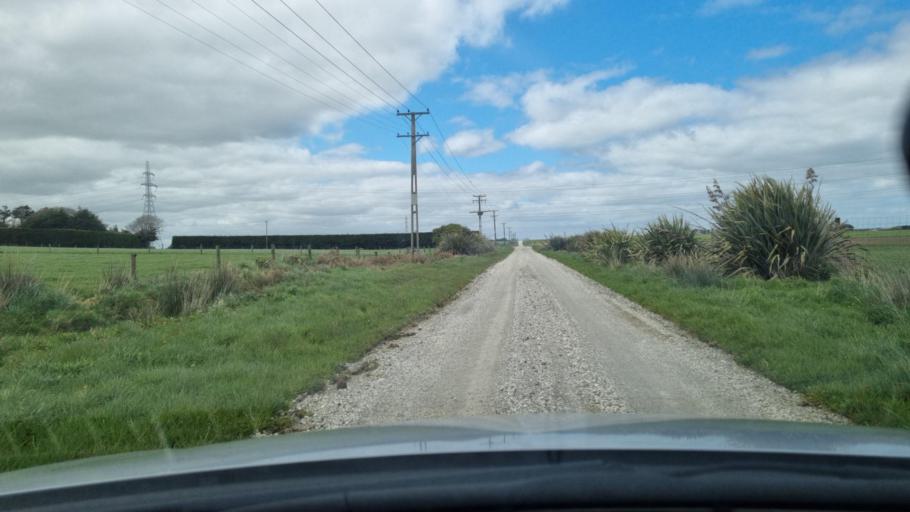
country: NZ
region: Southland
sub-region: Invercargill City
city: Invercargill
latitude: -46.4427
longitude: 168.4398
